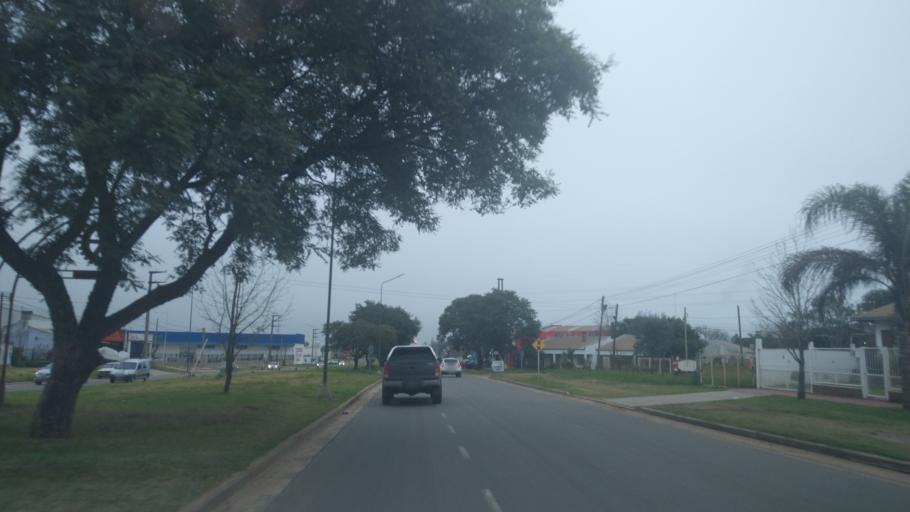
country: AR
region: Entre Rios
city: Chajari
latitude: -30.7617
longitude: -58.0094
